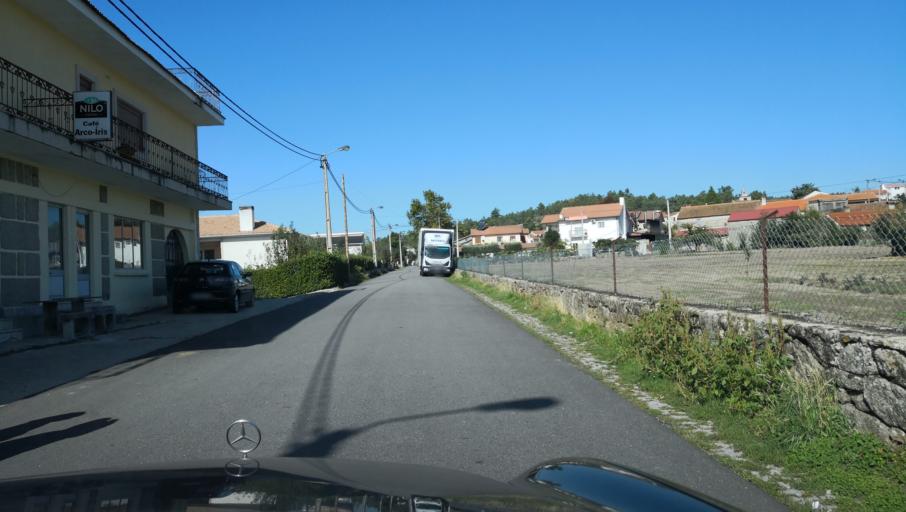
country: PT
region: Vila Real
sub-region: Sabrosa
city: Sabrosa
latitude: 41.3304
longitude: -7.6307
